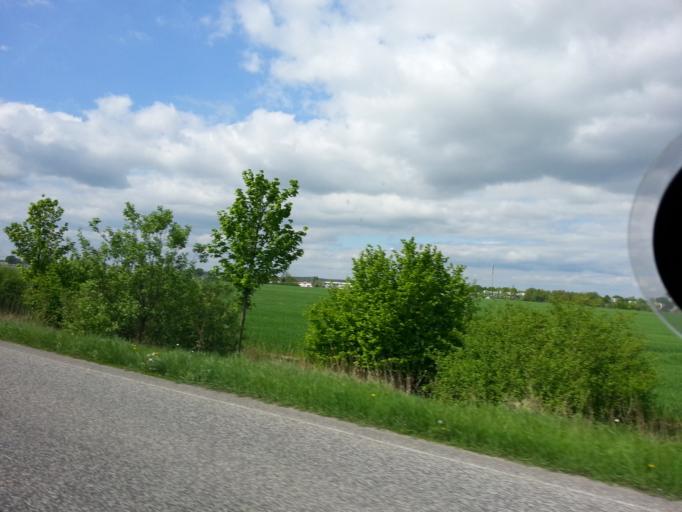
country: DE
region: Brandenburg
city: Werneuchen
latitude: 52.6112
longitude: 13.6738
